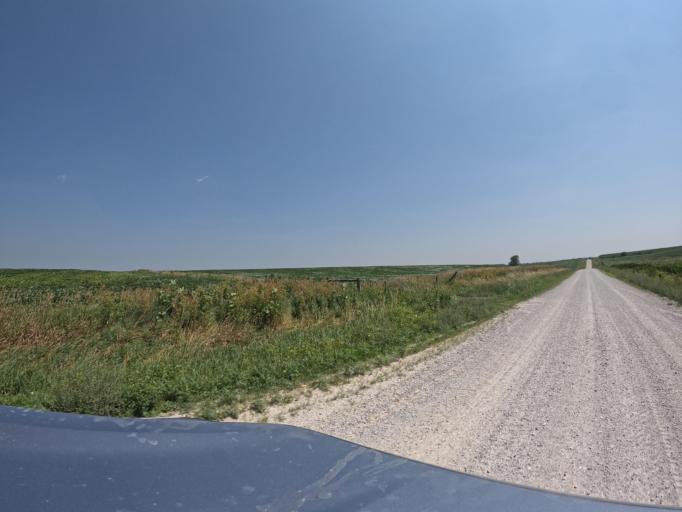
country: US
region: Iowa
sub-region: Keokuk County
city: Sigourney
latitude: 41.3337
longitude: -92.2385
